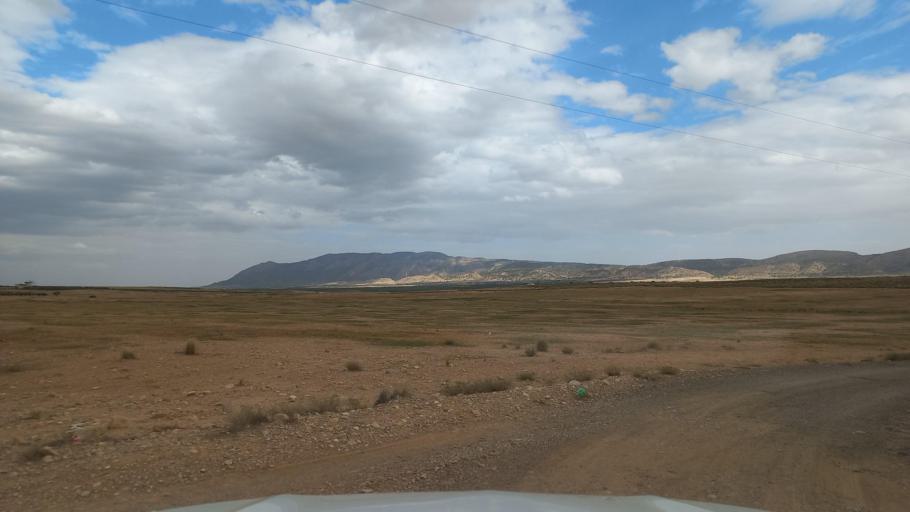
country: TN
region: Al Qasrayn
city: Sbiba
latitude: 35.3846
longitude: 9.1125
